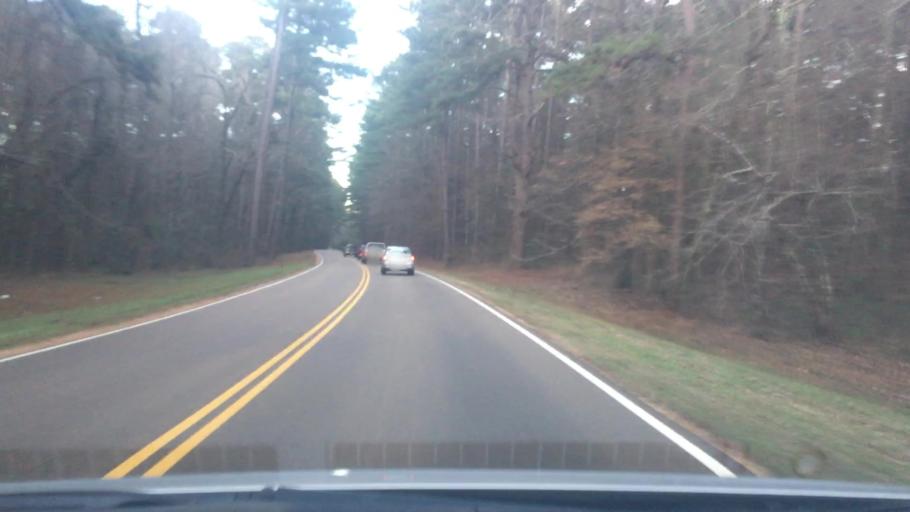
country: US
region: Mississippi
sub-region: Madison County
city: Canton
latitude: 32.5184
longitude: -89.9810
